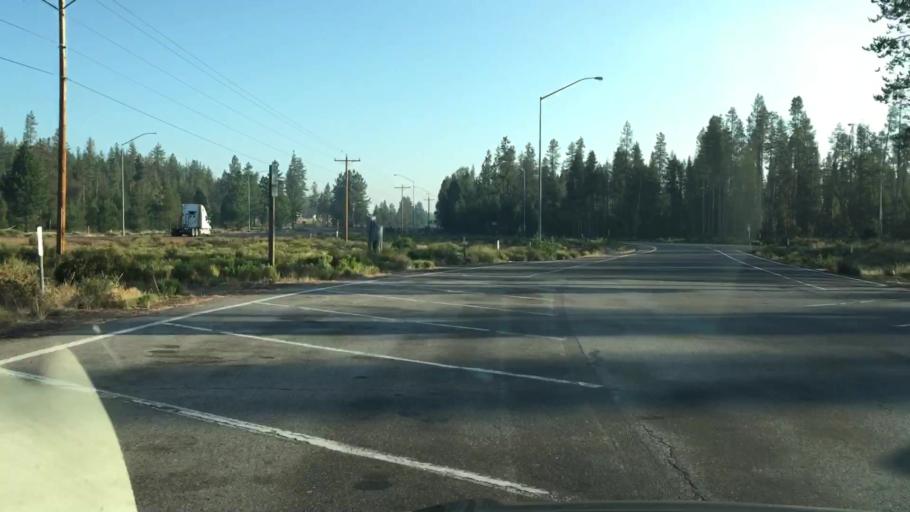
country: US
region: Oregon
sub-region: Deschutes County
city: La Pine
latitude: 43.1725
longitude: -121.7865
